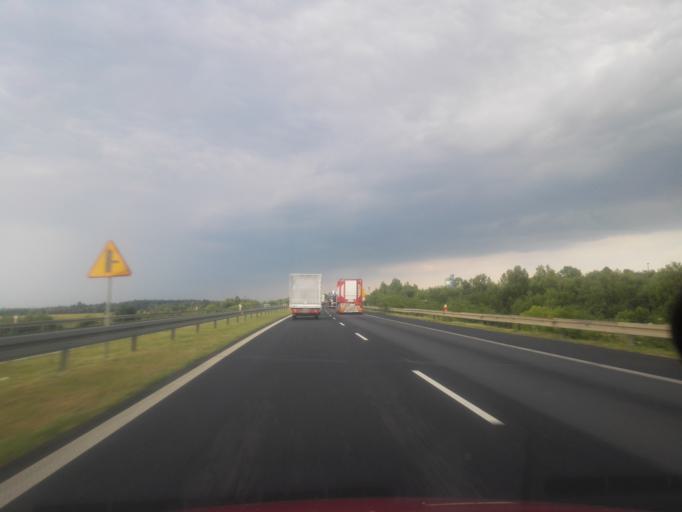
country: PL
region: Silesian Voivodeship
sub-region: Powiat czestochowski
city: Koscielec
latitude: 50.8842
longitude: 19.1696
